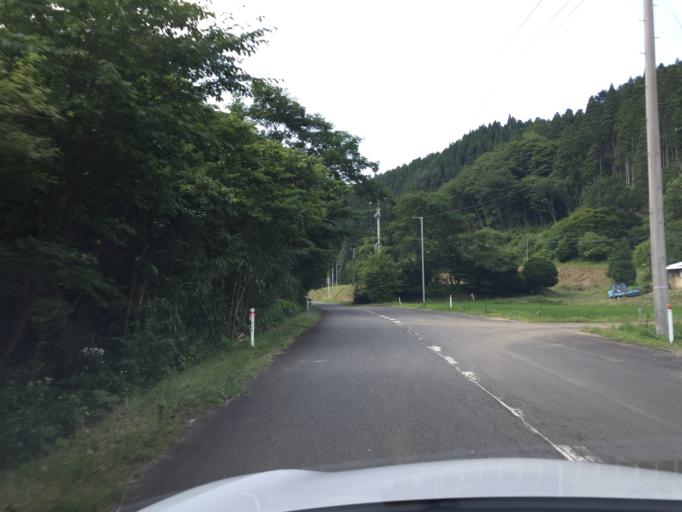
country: JP
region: Fukushima
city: Ishikawa
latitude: 37.1120
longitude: 140.6568
